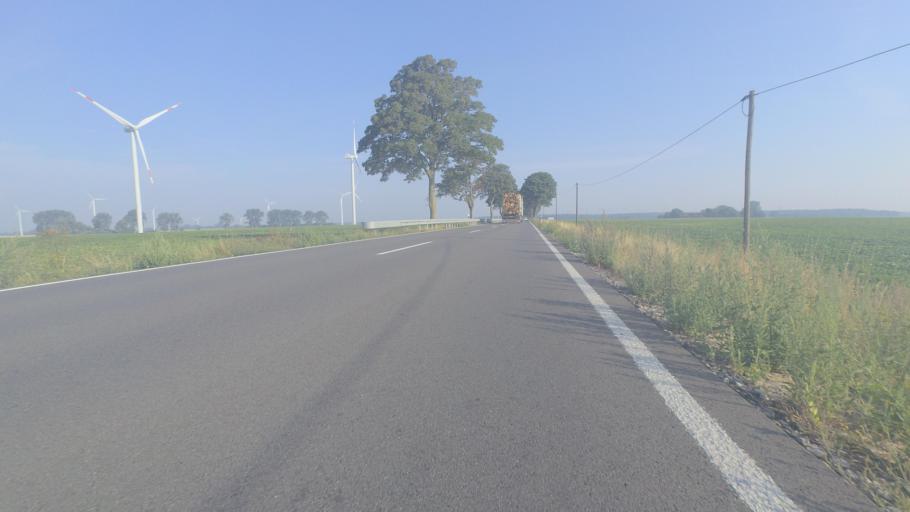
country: DE
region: Mecklenburg-Vorpommern
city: Gormin
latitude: 54.0046
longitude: 13.1438
